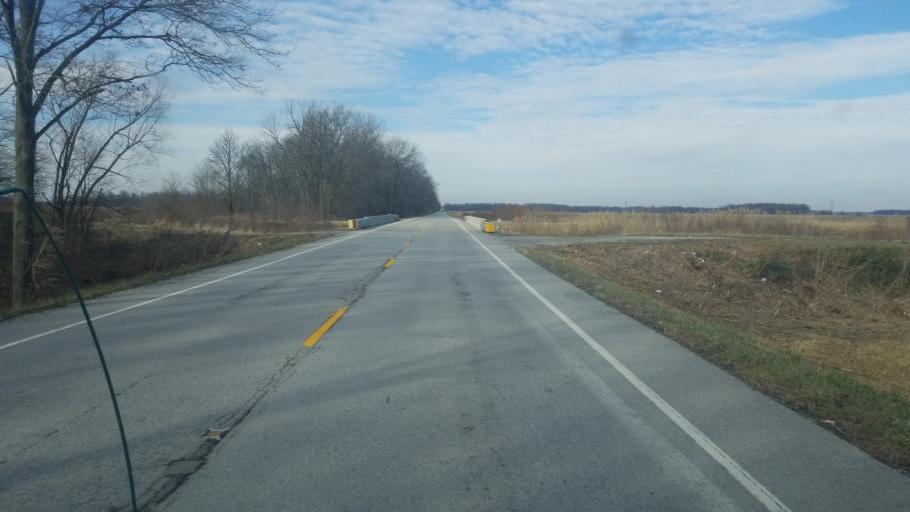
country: US
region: Illinois
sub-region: White County
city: Norris City
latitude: 37.9576
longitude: -88.4725
